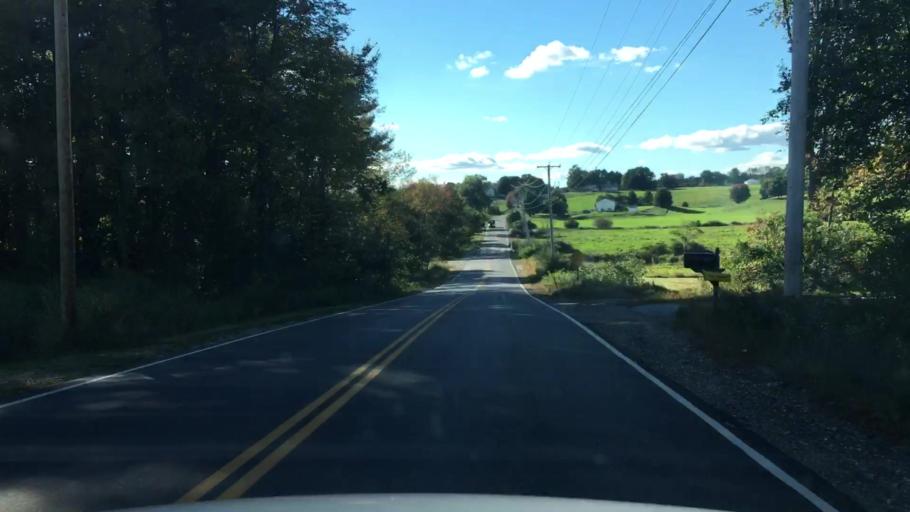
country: US
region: Maine
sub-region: Androscoggin County
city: Lisbon
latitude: 44.0748
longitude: -70.1021
